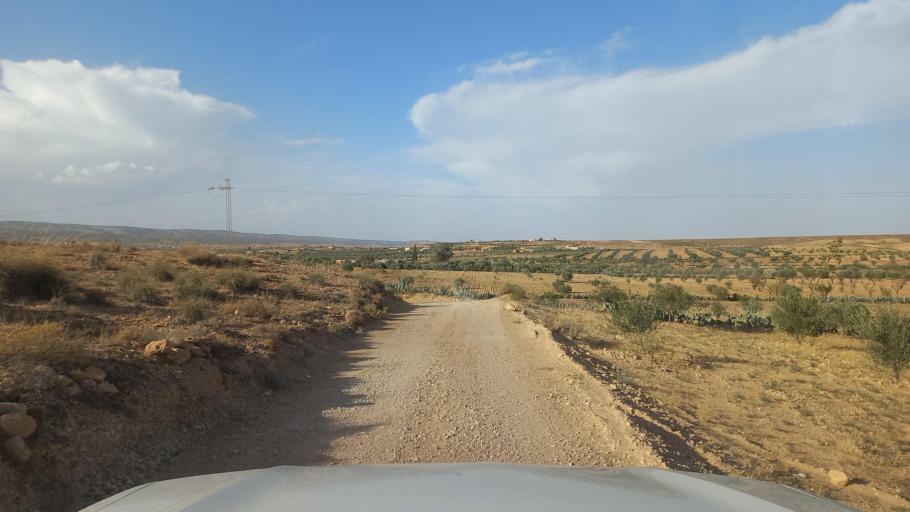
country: TN
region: Al Qasrayn
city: Kasserine
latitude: 35.2352
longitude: 8.9180
